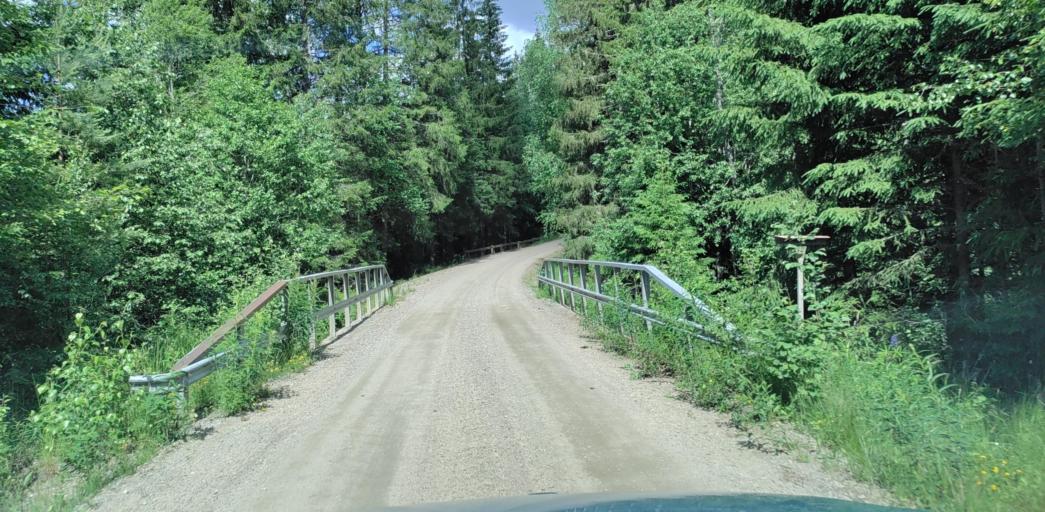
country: SE
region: Vaermland
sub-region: Hagfors Kommun
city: Ekshaerad
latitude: 60.0551
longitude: 13.2764
